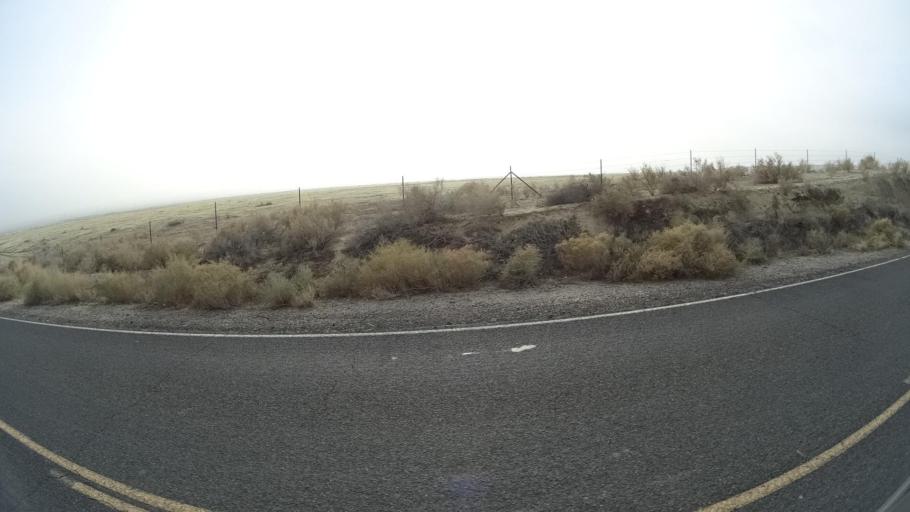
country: US
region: California
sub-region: Kern County
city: Ford City
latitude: 35.2394
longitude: -119.4501
